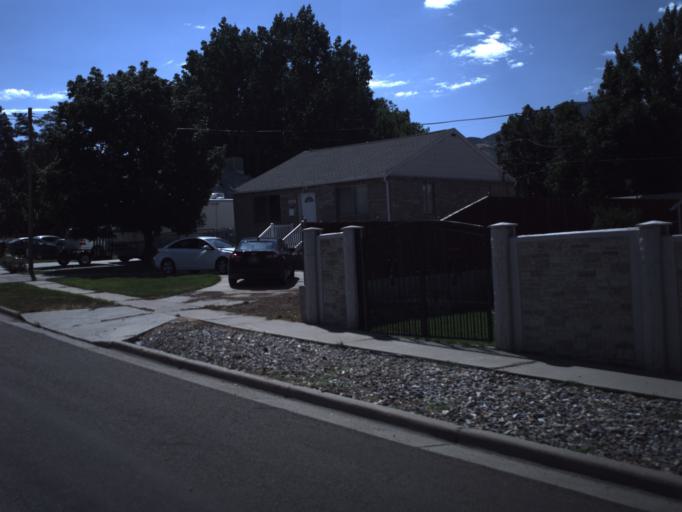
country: US
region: Utah
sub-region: Utah County
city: Spanish Fork
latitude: 40.1057
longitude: -111.6438
